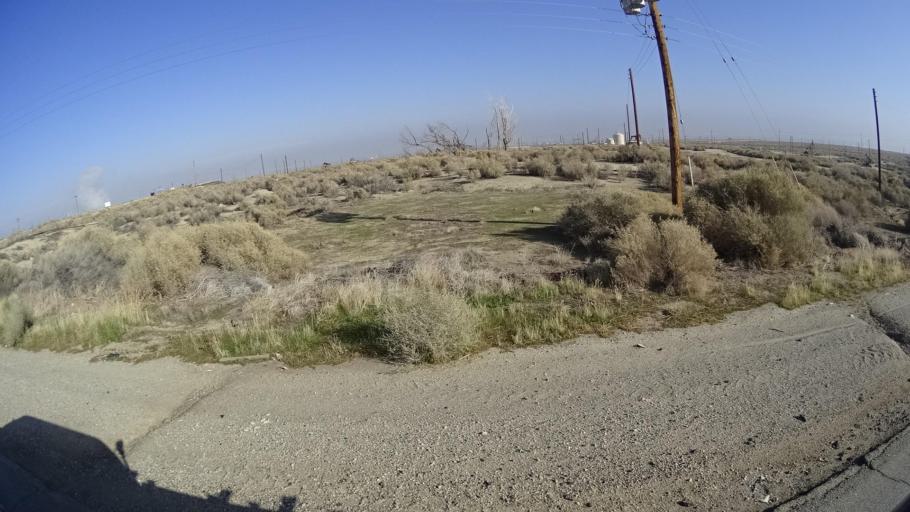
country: US
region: California
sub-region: Kern County
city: Taft Heights
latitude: 35.1910
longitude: -119.5753
